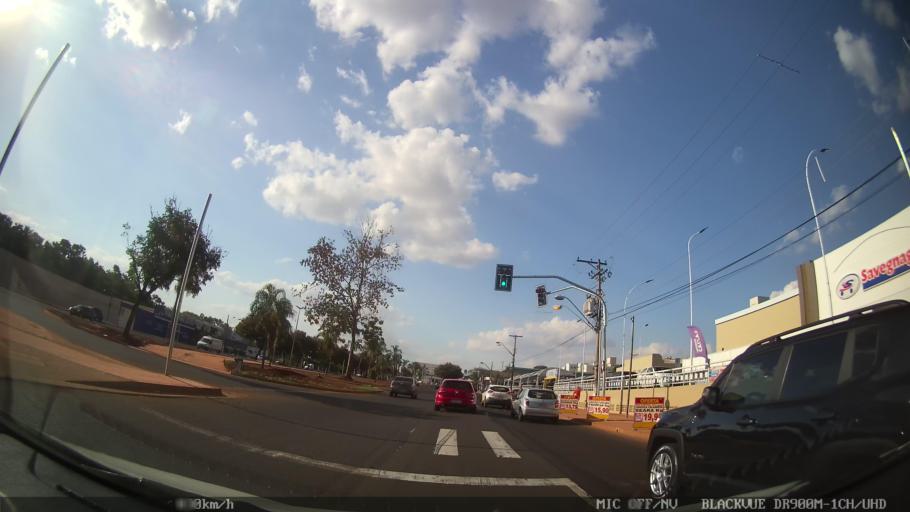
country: BR
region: Sao Paulo
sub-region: Ribeirao Preto
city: Ribeirao Preto
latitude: -21.1647
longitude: -47.8125
